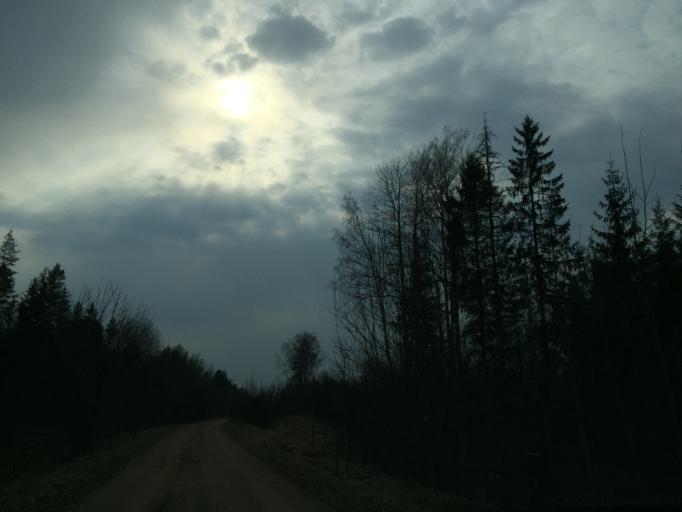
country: LV
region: Priekuli
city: Priekuli
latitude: 57.2031
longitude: 25.3870
